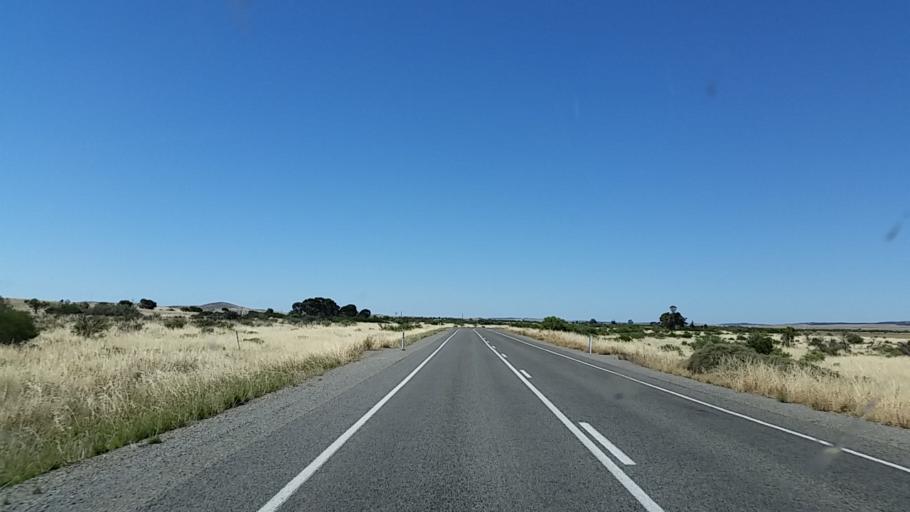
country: AU
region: South Australia
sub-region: Peterborough
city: Peterborough
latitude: -33.1753
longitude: 138.9089
